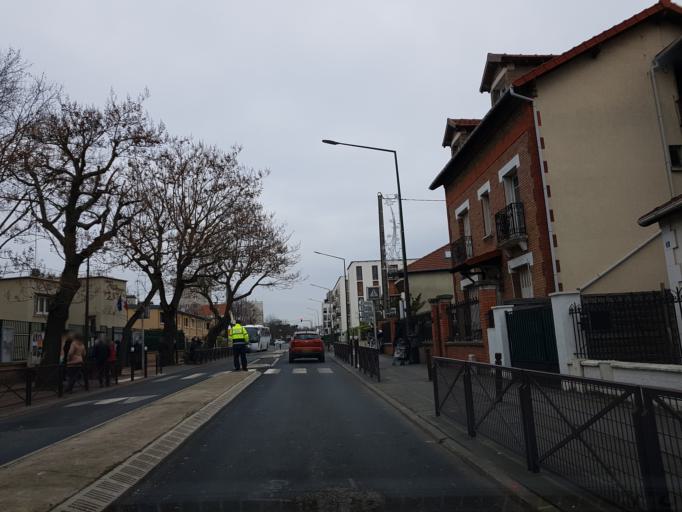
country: FR
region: Ile-de-France
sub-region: Departement du Val-de-Marne
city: Villejuif
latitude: 48.7859
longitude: 2.3544
